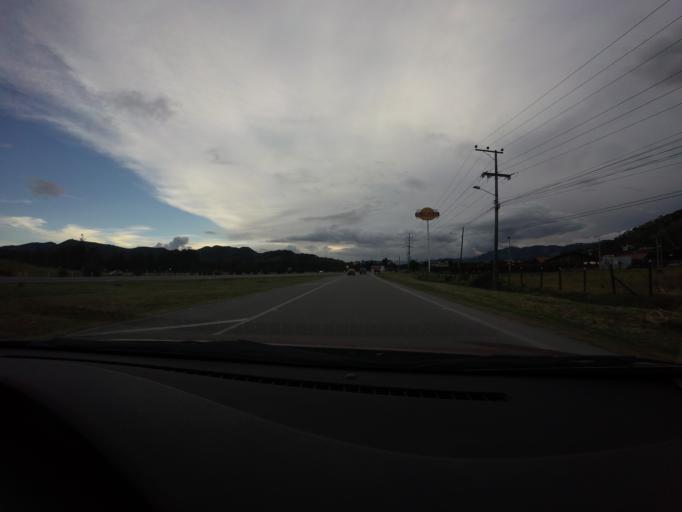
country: CO
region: Cundinamarca
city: Sopo
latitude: 4.9398
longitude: -73.9663
